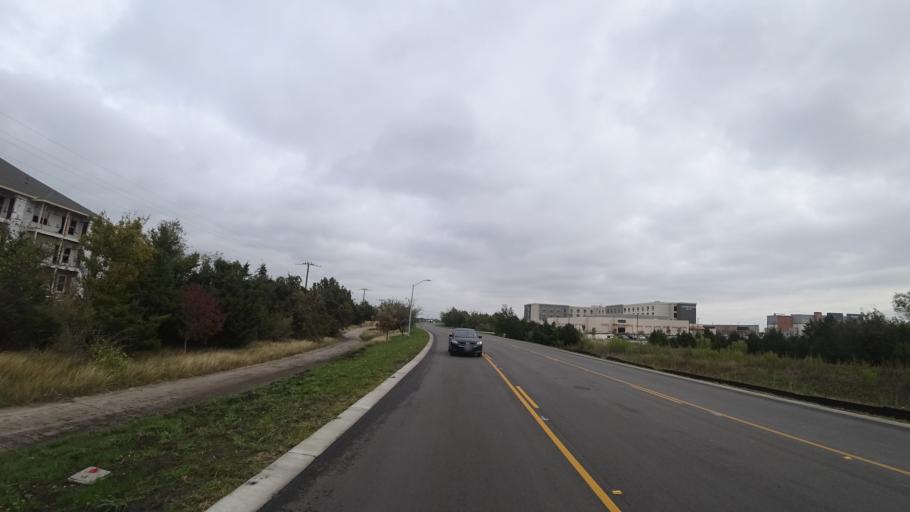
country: US
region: Texas
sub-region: Travis County
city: Pflugerville
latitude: 30.4218
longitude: -97.5928
